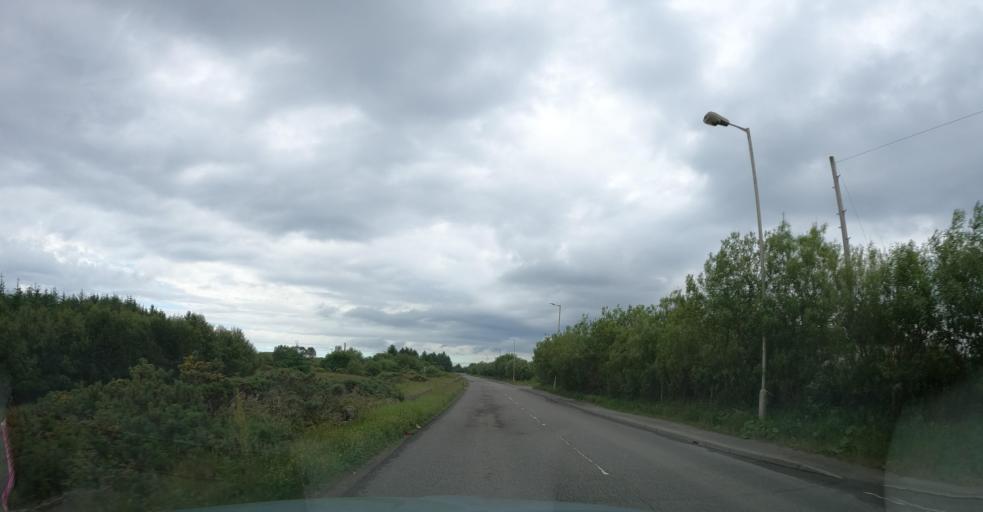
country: GB
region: Scotland
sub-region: Eilean Siar
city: Isle of Lewis
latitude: 58.2139
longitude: -6.4144
